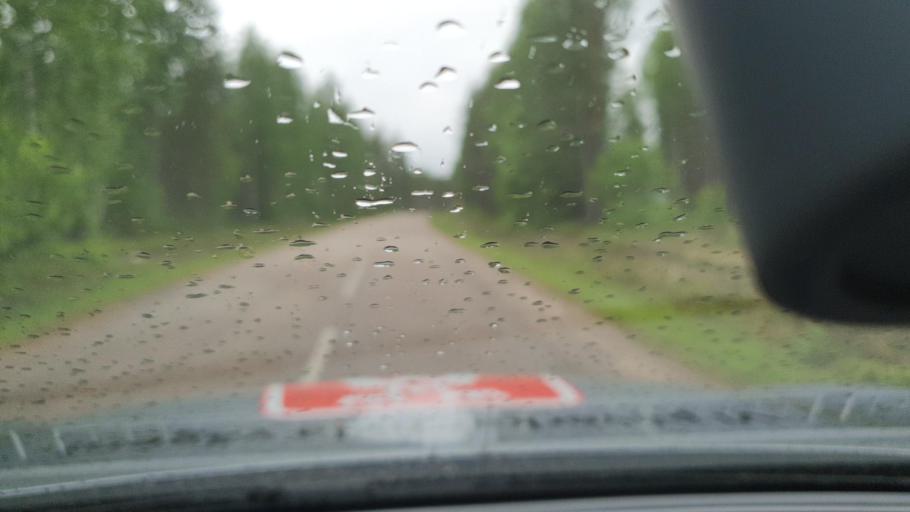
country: SE
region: Norrbotten
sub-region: Overkalix Kommun
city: OEverkalix
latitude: 66.4855
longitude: 22.7686
